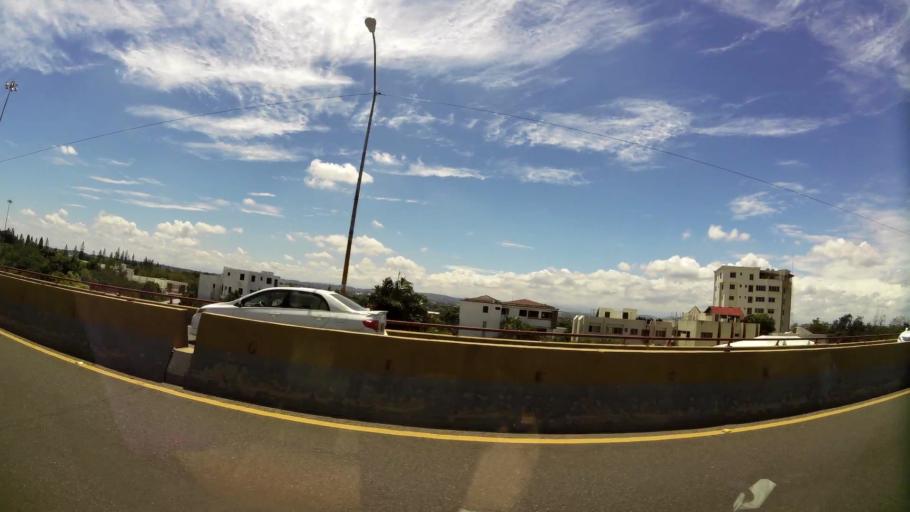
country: DO
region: Santiago
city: Santiago de los Caballeros
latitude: 19.4498
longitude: -70.6860
